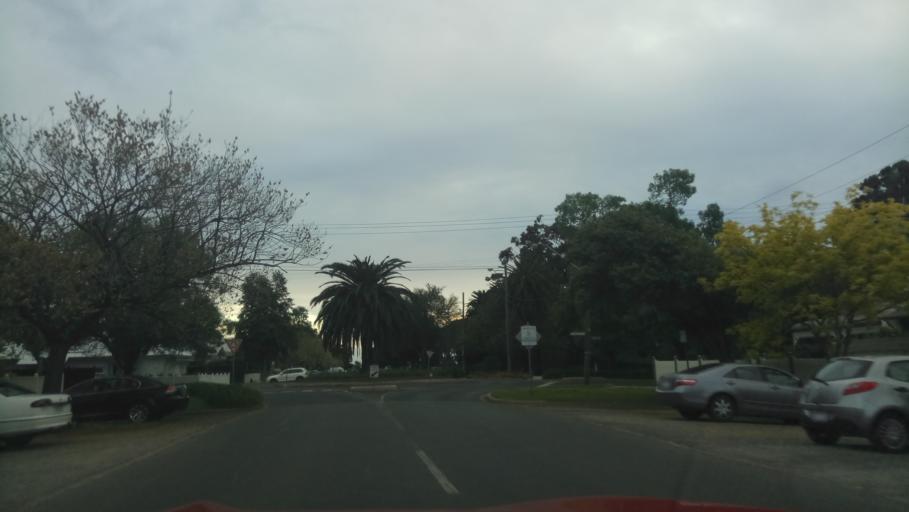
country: AU
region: Victoria
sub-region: Hobsons Bay
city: Williamstown
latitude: -37.8663
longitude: 144.8987
